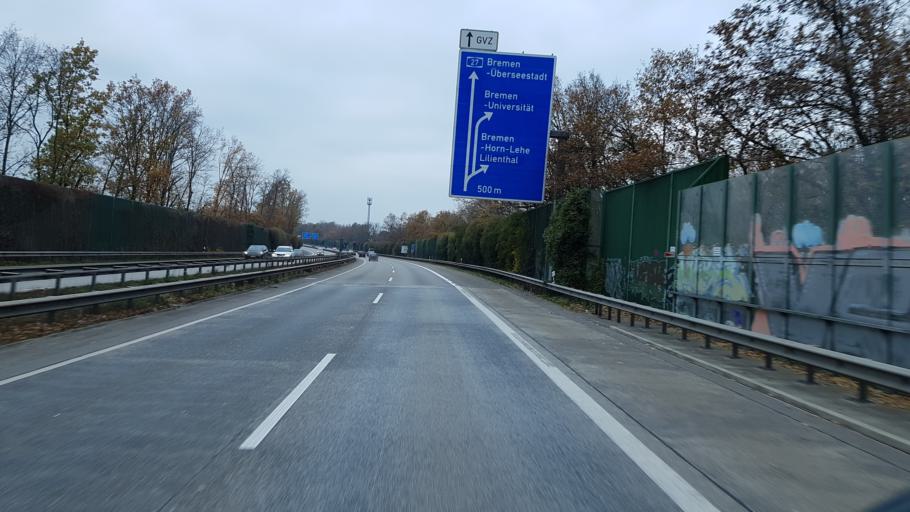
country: DE
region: Lower Saxony
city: Lilienthal
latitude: 53.1027
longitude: 8.8819
